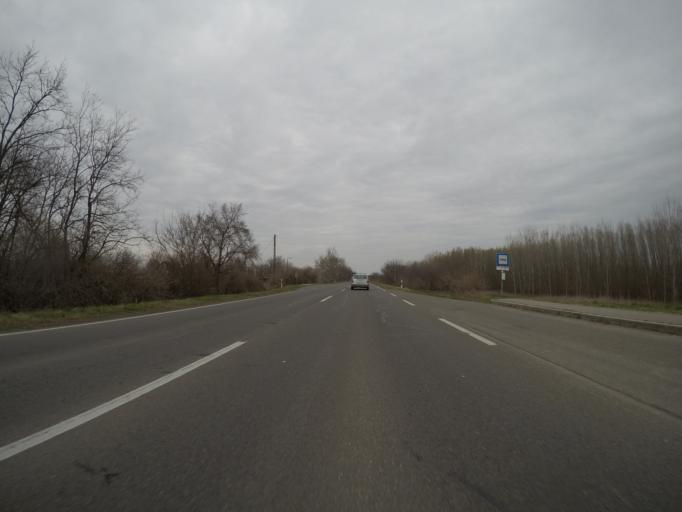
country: HU
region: Tolna
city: Dunaszentgyorgy
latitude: 46.5130
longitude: 18.7955
